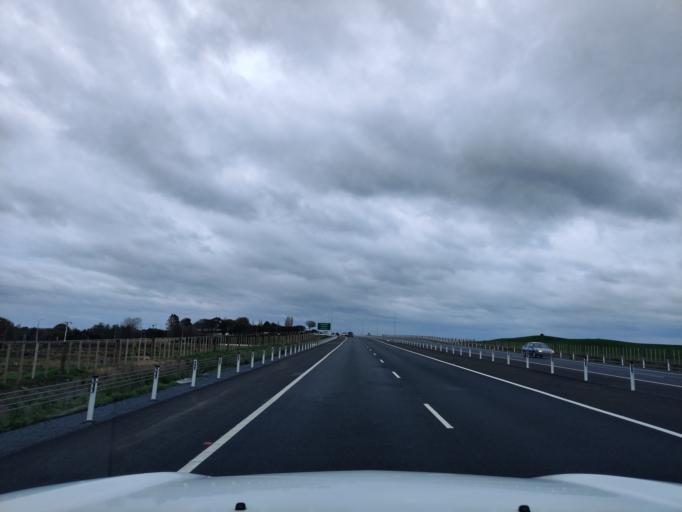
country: NZ
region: Waikato
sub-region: Waikato District
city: Te Kauwhata
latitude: -37.5130
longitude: 175.1689
